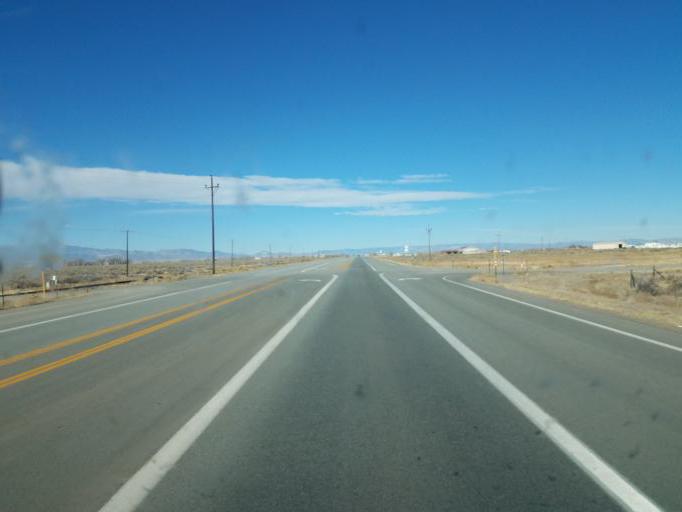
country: US
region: Colorado
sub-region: Alamosa County
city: Alamosa
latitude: 37.5130
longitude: -105.9837
